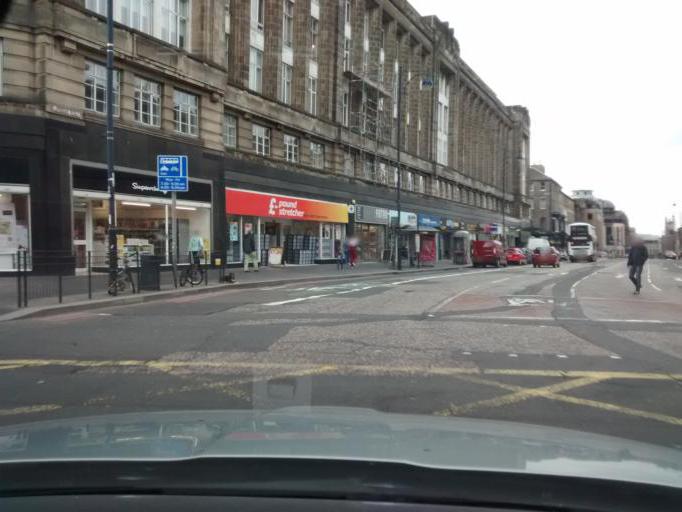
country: GB
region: Scotland
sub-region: Edinburgh
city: Edinburgh
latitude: 55.9448
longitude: -3.2051
